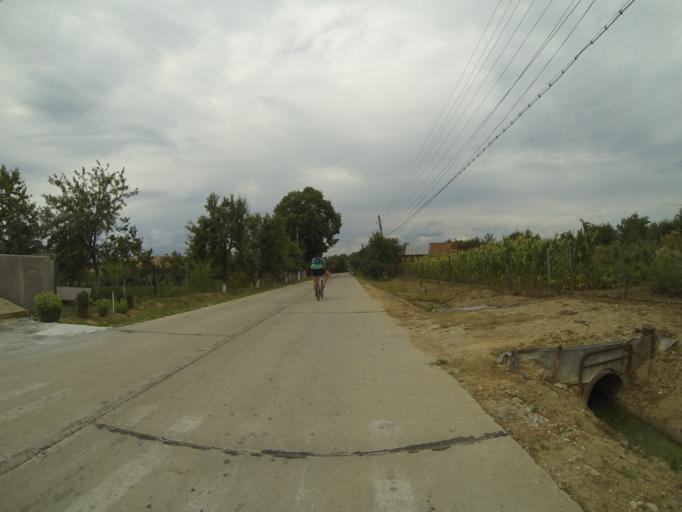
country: RO
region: Dolj
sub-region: Comuna Almaju
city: Almaju
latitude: 44.4293
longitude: 23.7056
